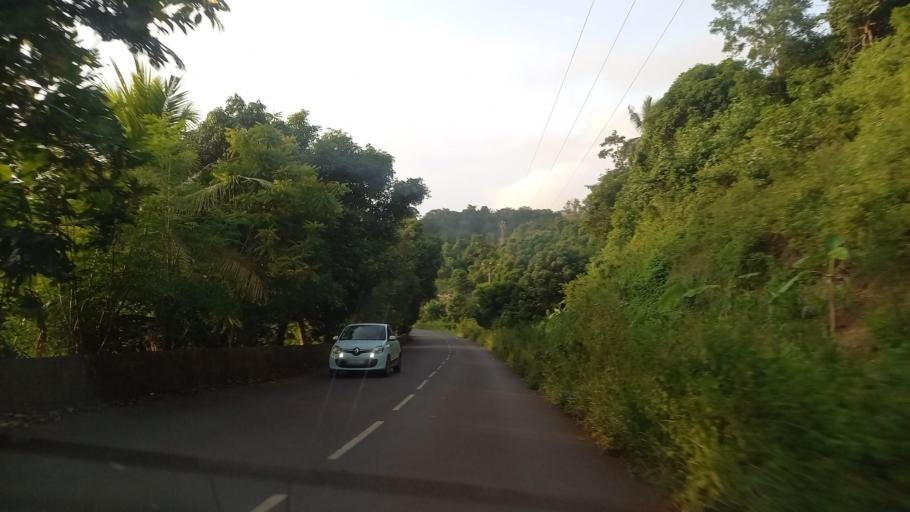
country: YT
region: M'Tsangamouji
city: M'Tsangamouji
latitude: -12.7629
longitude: 45.0749
